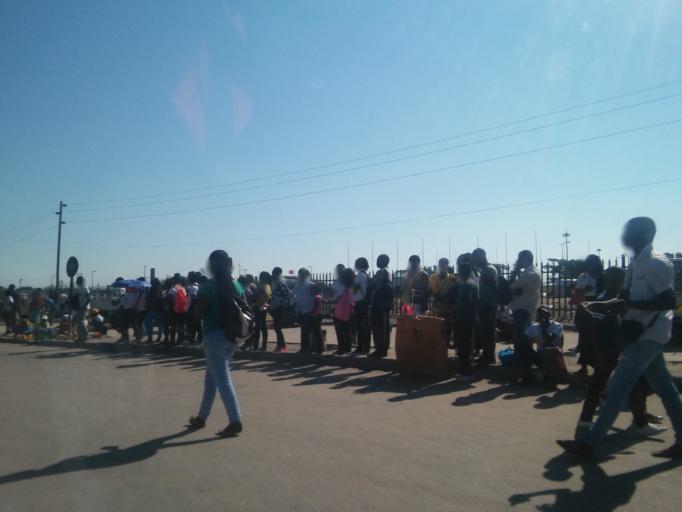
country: MZ
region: Maputo City
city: Maputo
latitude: -25.8303
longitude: 32.5737
